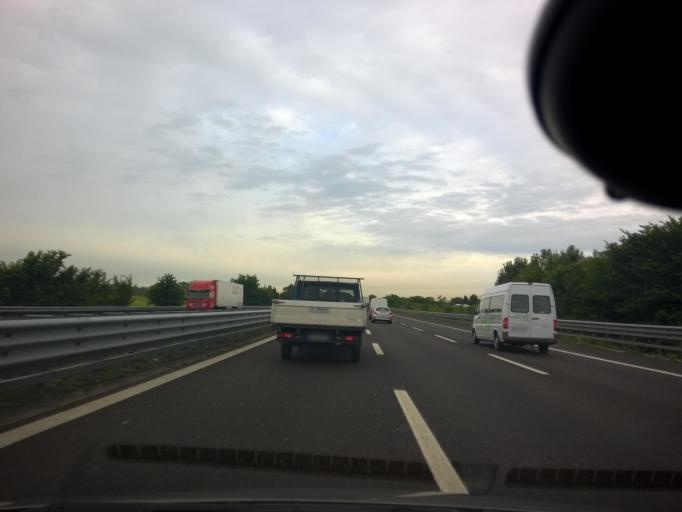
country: IT
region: Lombardy
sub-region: Provincia di Brescia
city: Pozzolengo
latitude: 45.4329
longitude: 10.6296
